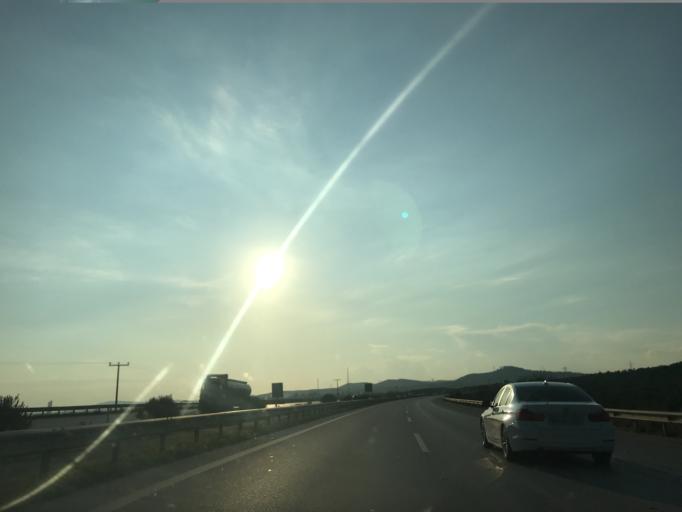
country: TR
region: Osmaniye
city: Toprakkale
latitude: 36.9674
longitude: 36.0482
